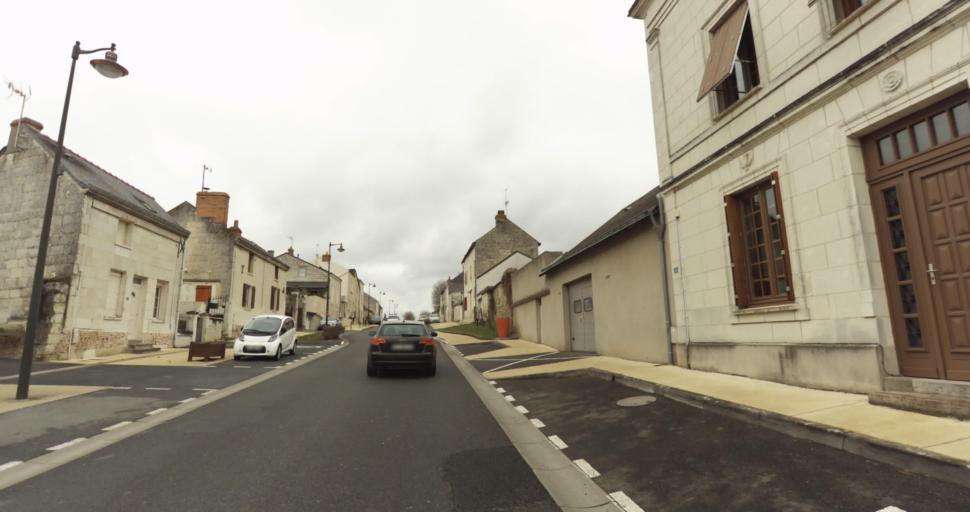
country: FR
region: Pays de la Loire
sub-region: Departement de Maine-et-Loire
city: Distre
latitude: 47.2232
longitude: -0.1109
